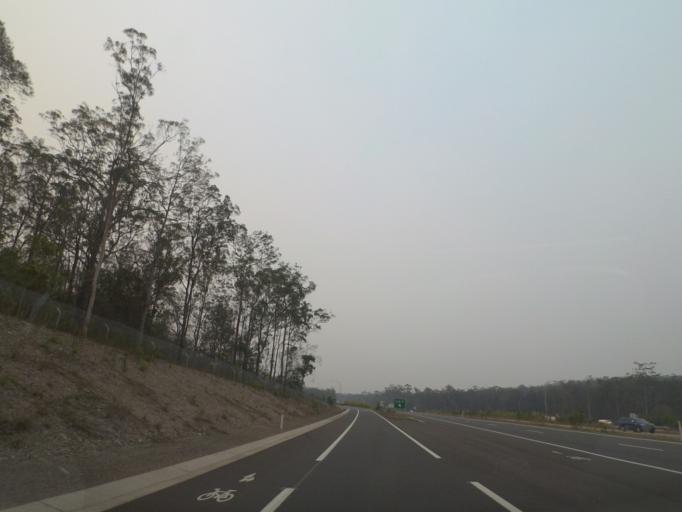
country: AU
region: New South Wales
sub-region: Kempsey
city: Crescent Head
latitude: -31.2506
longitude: 152.8204
